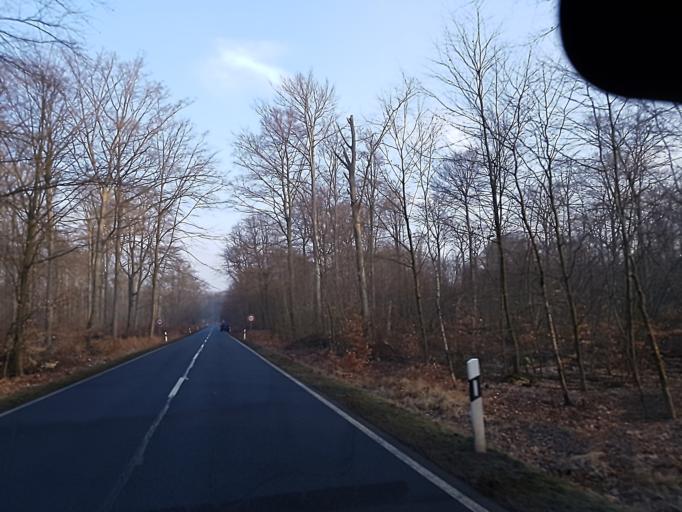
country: DE
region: Brandenburg
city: Wiesenburg
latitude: 52.0220
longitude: 12.4604
